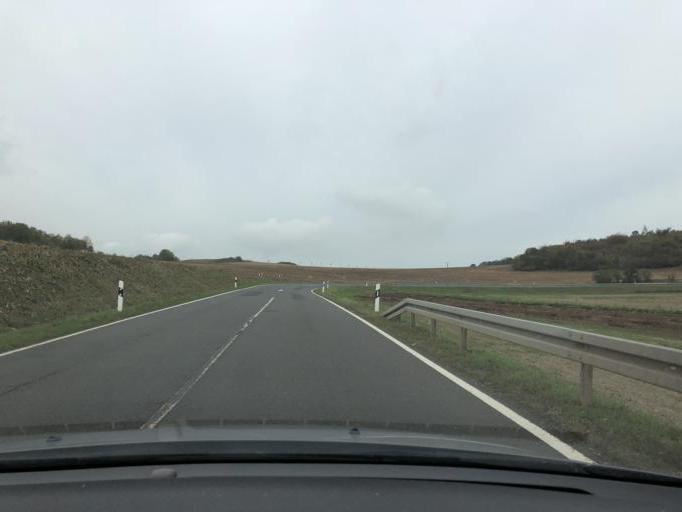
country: DE
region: Thuringia
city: Auleben
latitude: 51.4100
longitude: 10.9755
